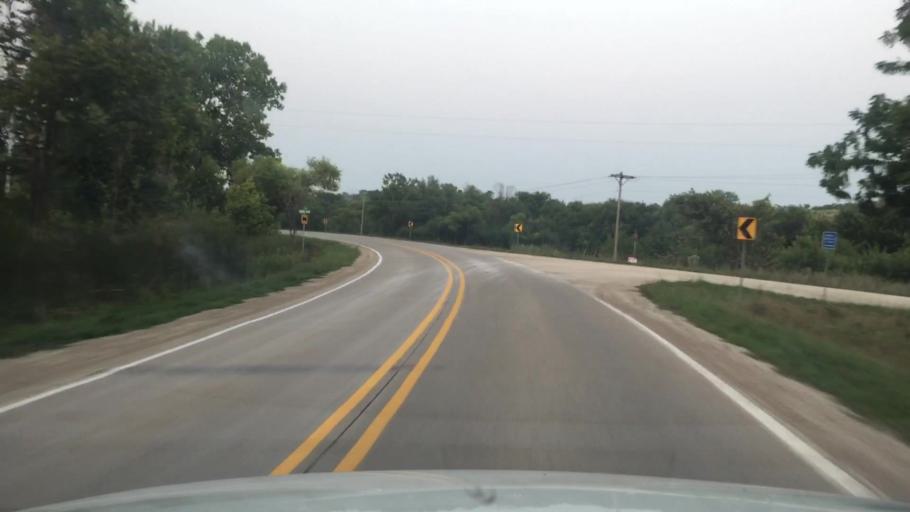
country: US
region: Iowa
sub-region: Clarke County
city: Osceola
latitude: 41.1803
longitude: -93.7124
